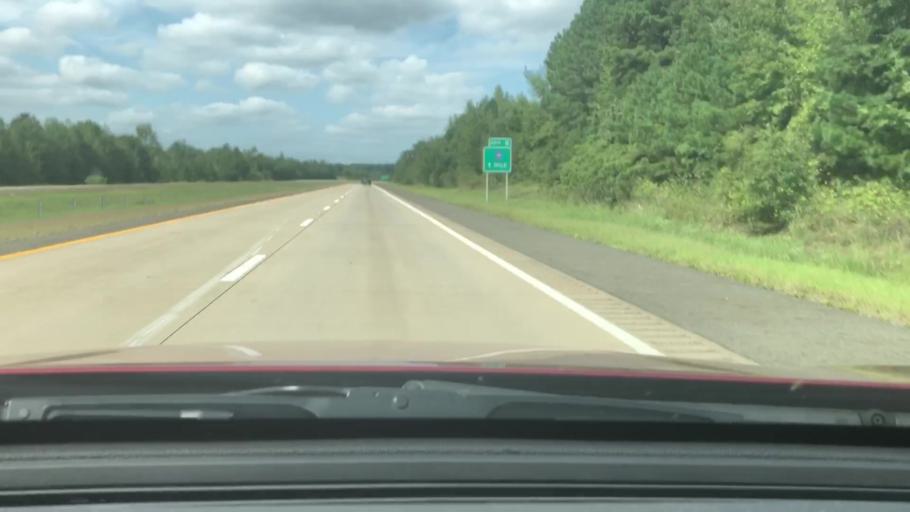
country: US
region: Louisiana
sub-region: Caddo Parish
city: Vivian
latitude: 33.1001
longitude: -93.8956
